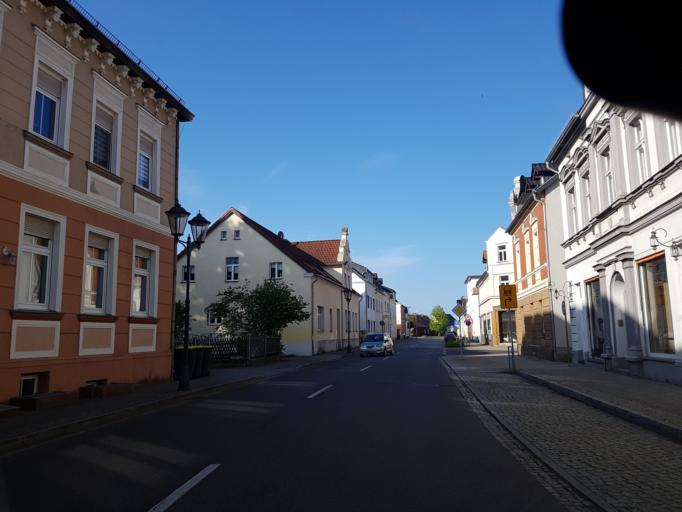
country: DE
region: Brandenburg
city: Altdobern
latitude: 51.6499
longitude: 14.0325
